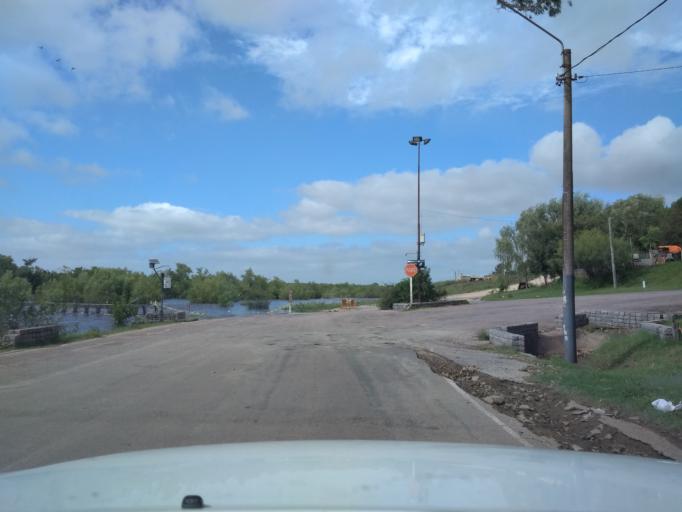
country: UY
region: Florida
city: Florida
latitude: -34.1073
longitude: -56.2053
